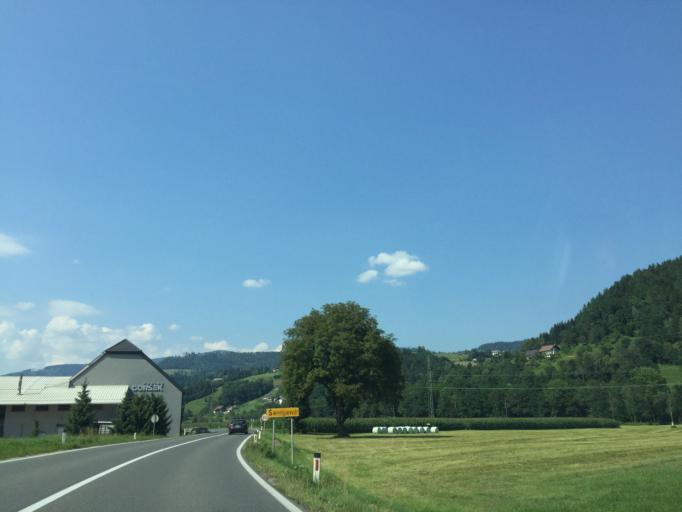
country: SI
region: Slovenj Gradec
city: Pamece
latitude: 46.5550
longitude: 15.0440
